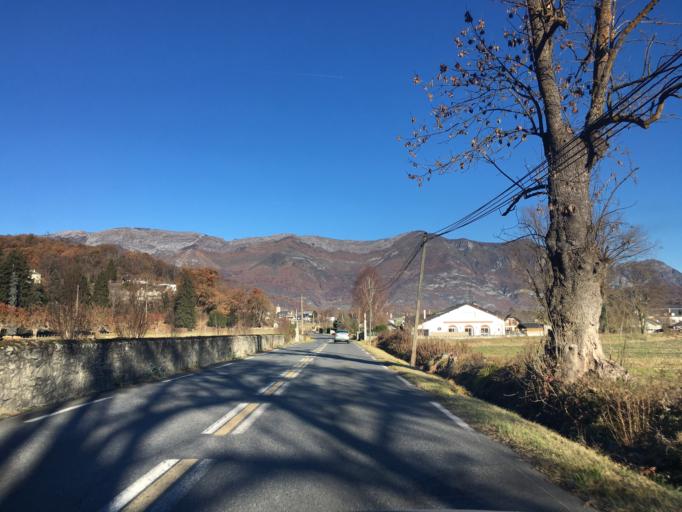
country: FR
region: Midi-Pyrenees
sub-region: Departement des Hautes-Pyrenees
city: Argeles-Gazost
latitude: 42.9900
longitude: -0.0897
